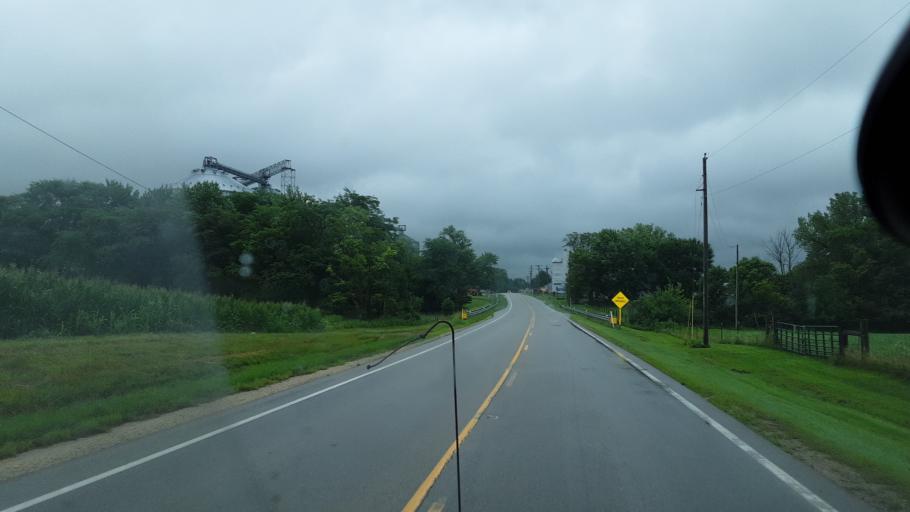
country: US
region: Indiana
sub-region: Adams County
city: Decatur
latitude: 40.7521
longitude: -84.8015
